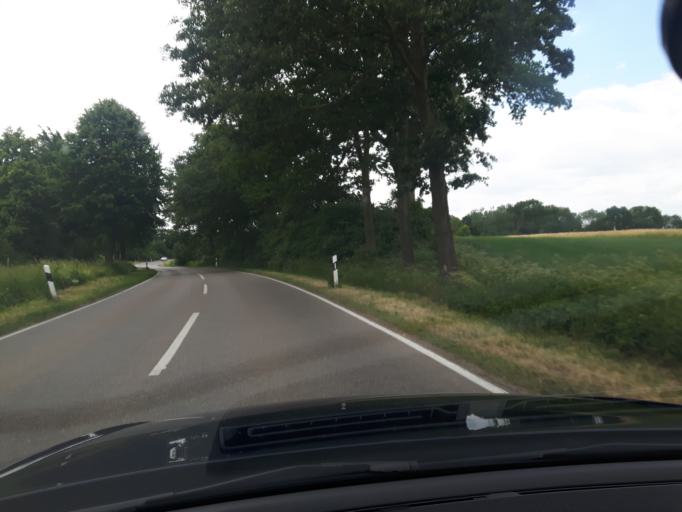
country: DE
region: Schleswig-Holstein
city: Sierksdorf
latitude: 54.0907
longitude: 10.7802
